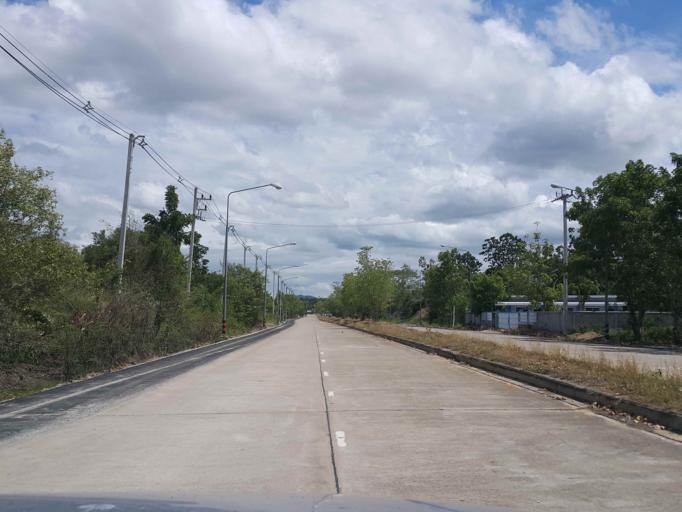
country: TH
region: Tak
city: Tak
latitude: 16.8606
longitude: 99.1149
